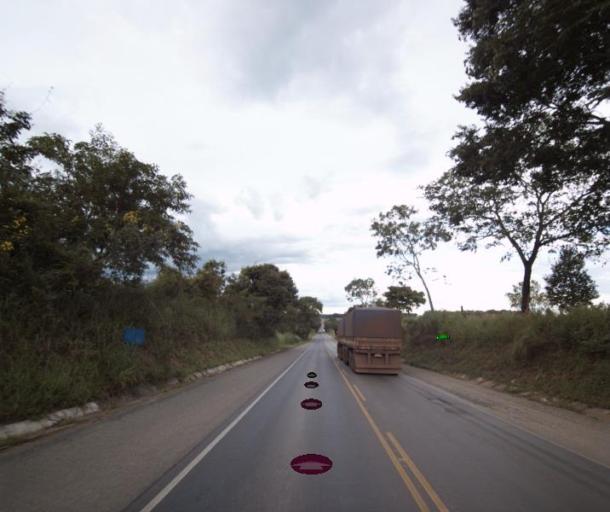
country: BR
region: Goias
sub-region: Itapaci
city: Itapaci
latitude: -15.0358
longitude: -49.4363
